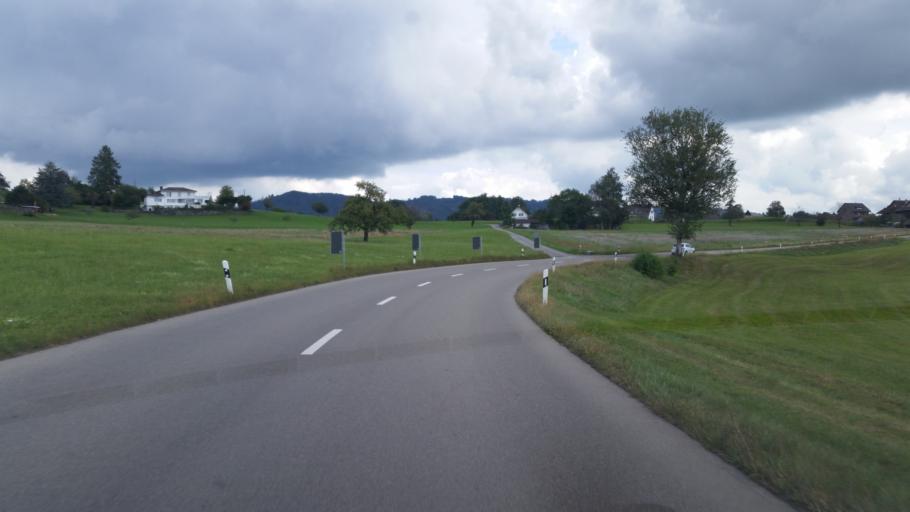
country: CH
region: Zurich
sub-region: Bezirk Affoltern
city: Mettmenstetten
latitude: 47.2438
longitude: 8.4881
